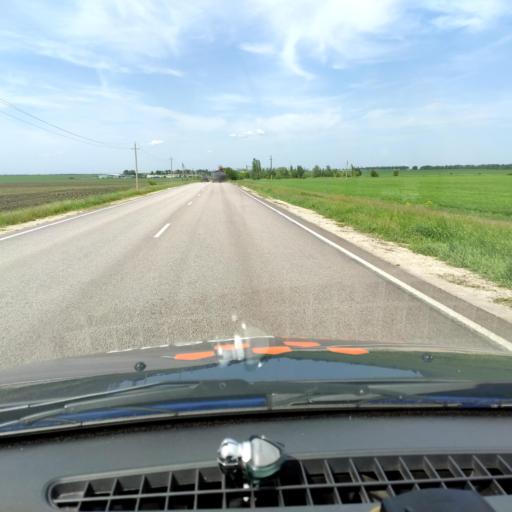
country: RU
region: Voronezj
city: Novaya Usman'
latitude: 51.5666
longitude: 39.3756
